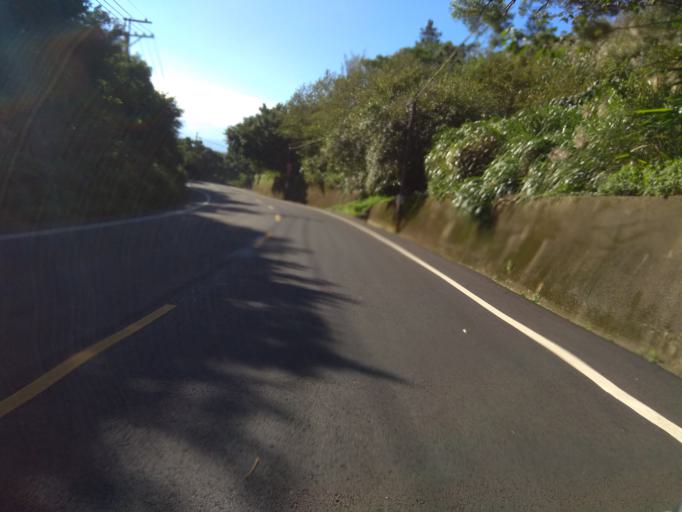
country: TW
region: Taiwan
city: Daxi
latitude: 24.8659
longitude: 121.1554
